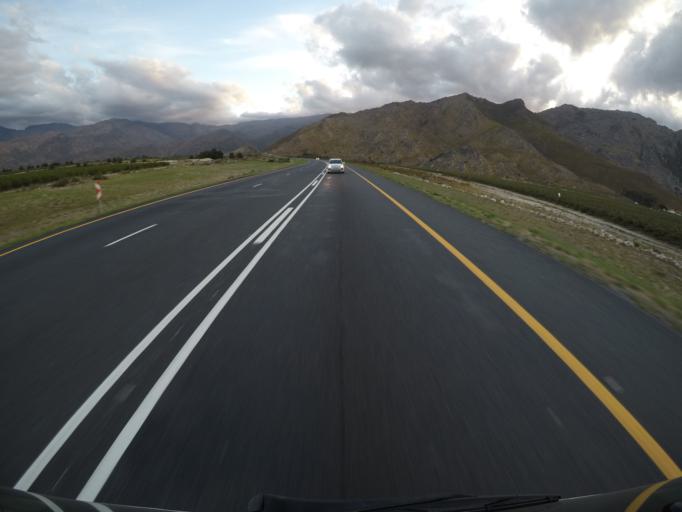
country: ZA
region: Western Cape
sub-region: Cape Winelands District Municipality
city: Worcester
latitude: -33.6872
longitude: 19.2718
